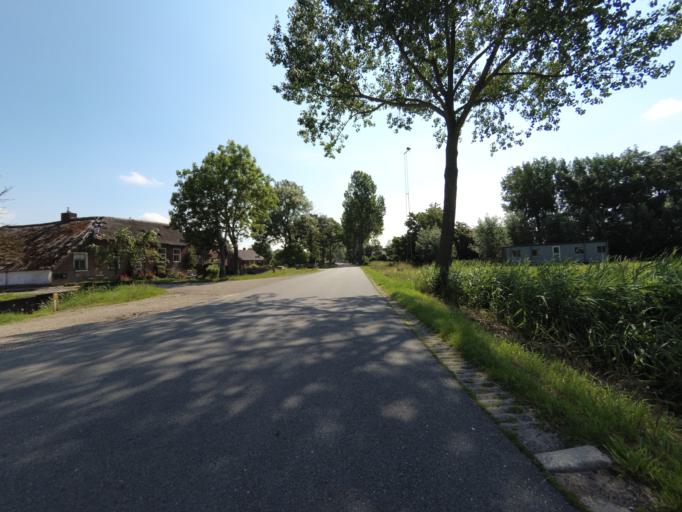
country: NL
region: Utrecht
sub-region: Gemeente Vianen
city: Vianen
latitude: 51.9491
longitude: 5.0523
